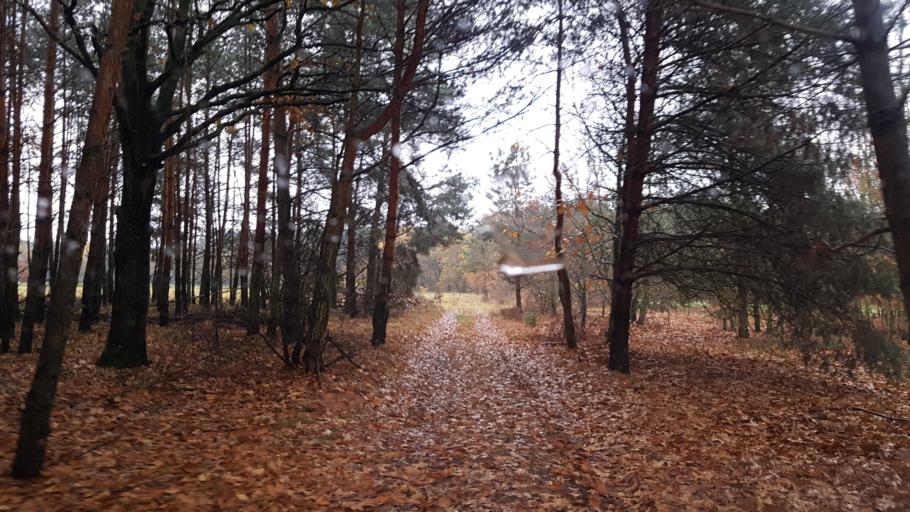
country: DE
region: Brandenburg
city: Altdobern
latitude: 51.6937
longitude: 14.0474
